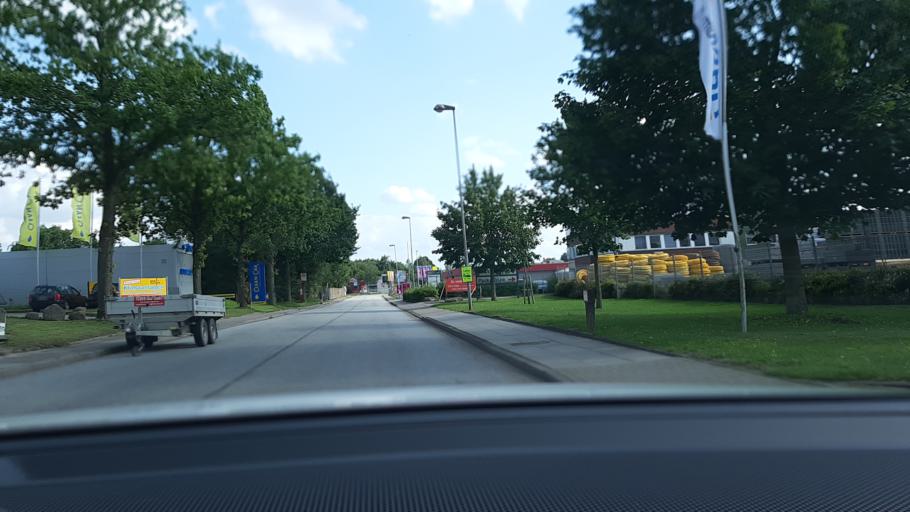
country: DE
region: Schleswig-Holstein
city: Politz
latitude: 53.8024
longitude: 10.4026
